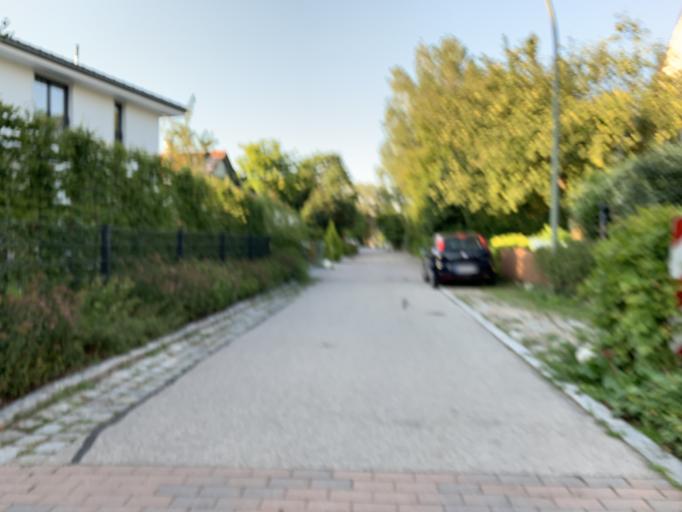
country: DE
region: Bavaria
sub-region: Upper Bavaria
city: Freising
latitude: 48.3903
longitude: 11.7286
